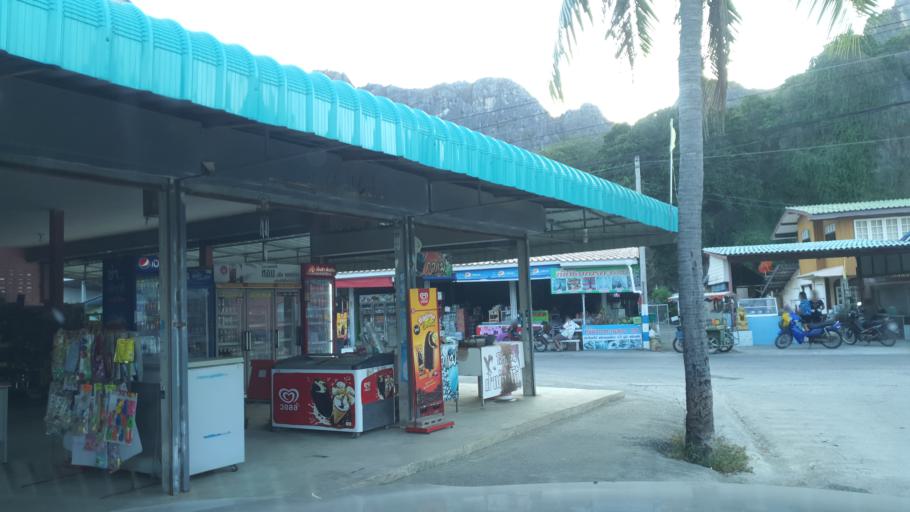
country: TH
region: Prachuap Khiri Khan
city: Sam Roi Yot
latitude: 12.2028
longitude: 100.0057
